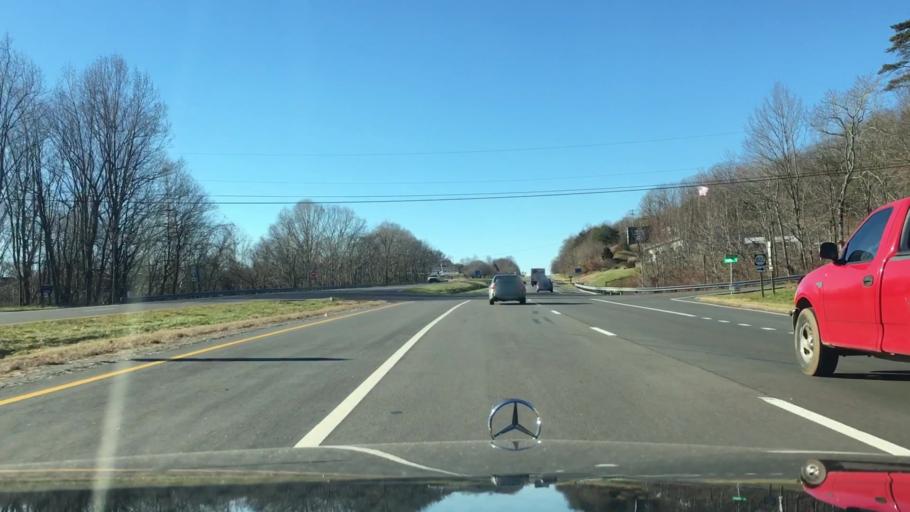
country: US
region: Virginia
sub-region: Roanoke County
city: Vinton
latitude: 37.2718
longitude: -79.8087
